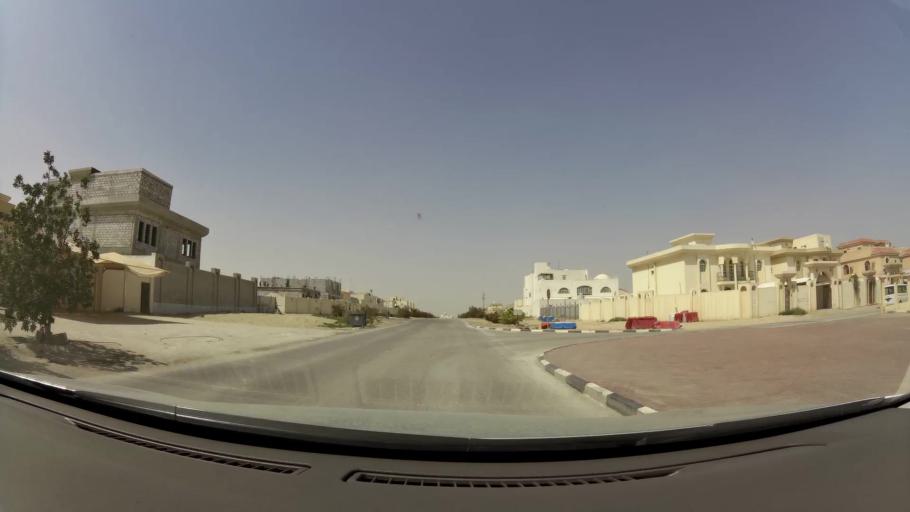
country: QA
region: Baladiyat Umm Salal
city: Umm Salal Muhammad
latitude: 25.3817
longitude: 51.4189
